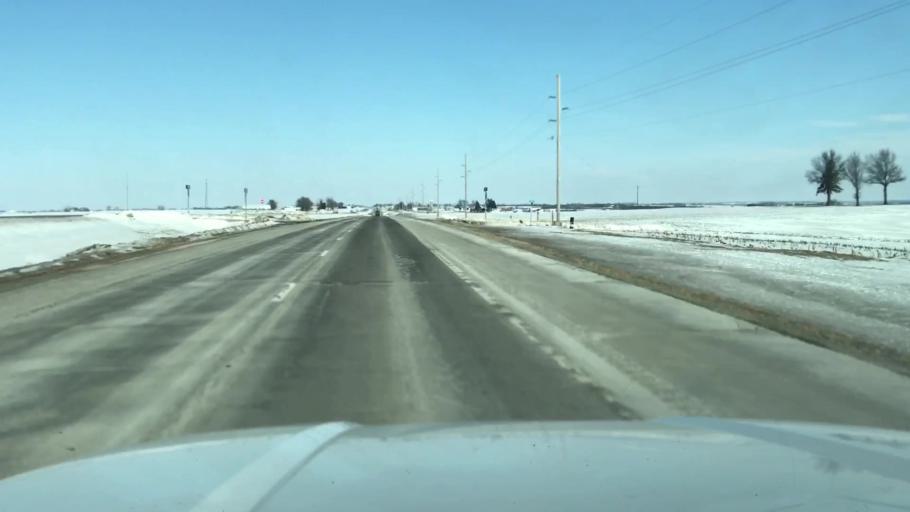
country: US
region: Missouri
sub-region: Nodaway County
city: Maryville
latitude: 40.2287
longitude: -94.8677
